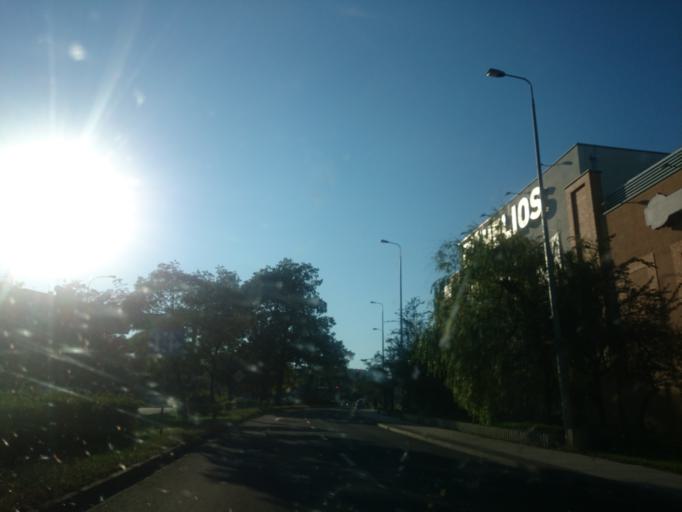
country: PL
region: Lubusz
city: Gorzow Wielkopolski
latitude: 52.7306
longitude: 15.2253
